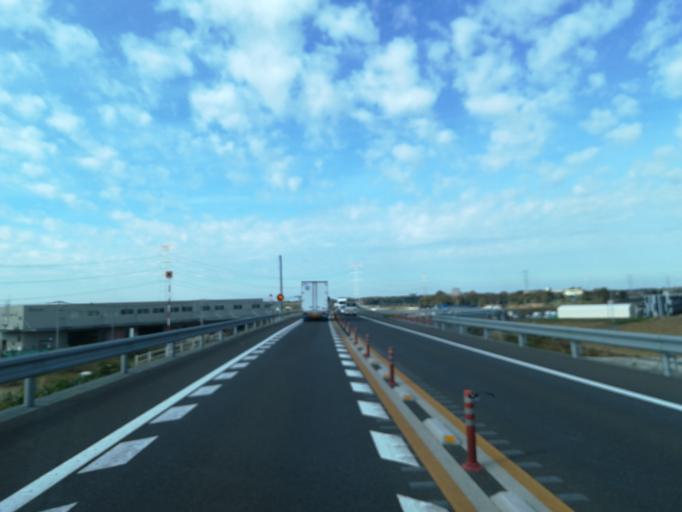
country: JP
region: Ibaraki
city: Mitsukaido
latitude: 36.0571
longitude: 140.0479
